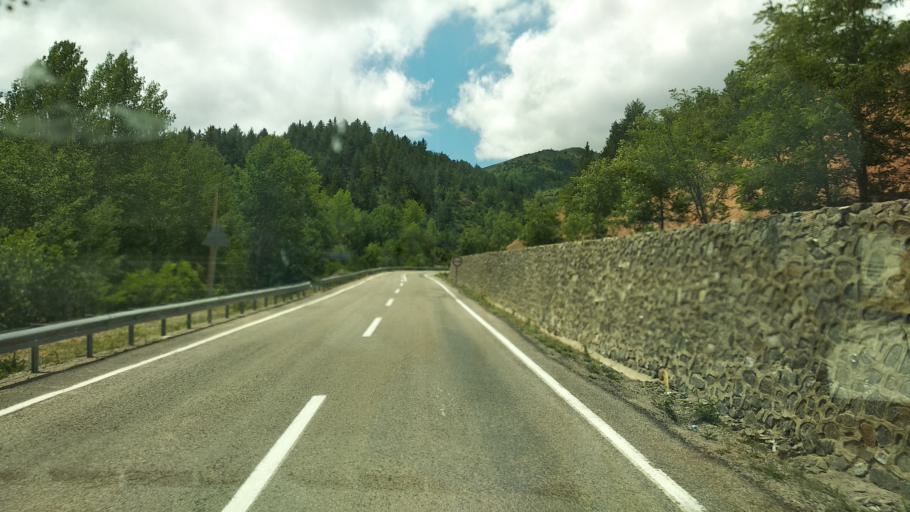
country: TR
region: Gumushane
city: Kose
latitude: 40.3025
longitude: 39.5561
